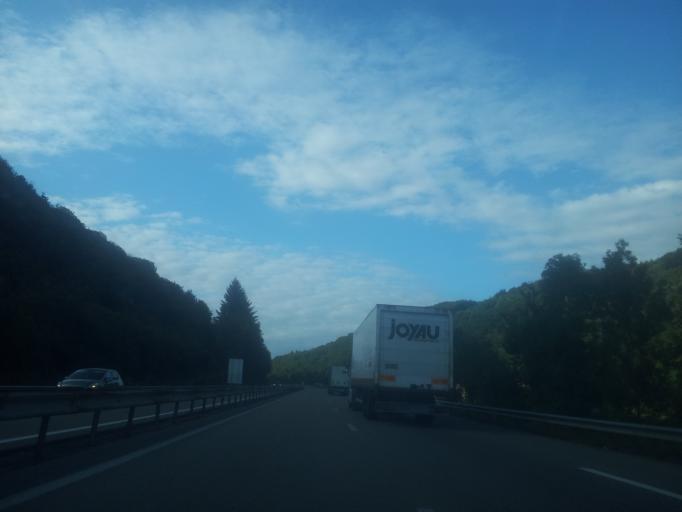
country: FR
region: Rhone-Alpes
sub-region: Departement de l'Isere
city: Colombe
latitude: 45.4064
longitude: 5.4640
